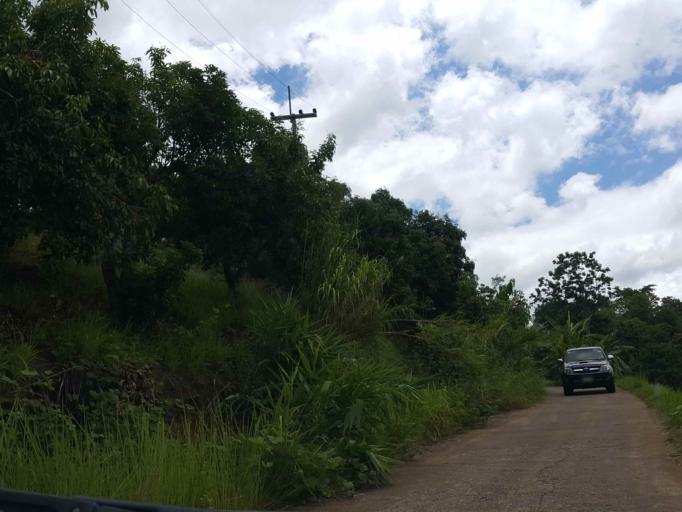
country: TH
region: Chiang Mai
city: Hang Dong
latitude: 18.7775
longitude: 98.8378
